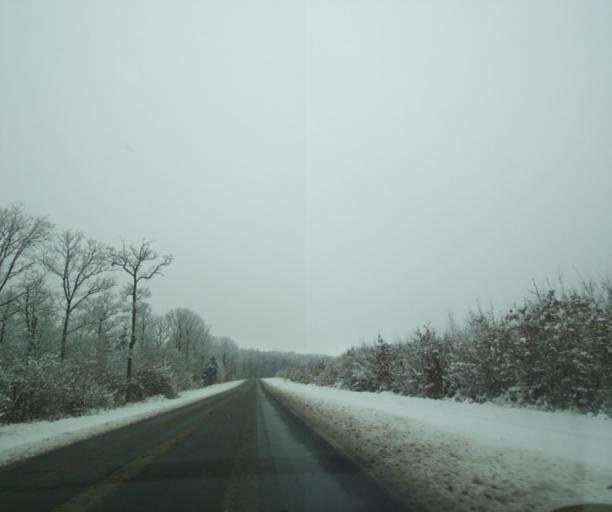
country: FR
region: Champagne-Ardenne
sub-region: Departement de la Haute-Marne
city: Laneuville-a-Remy
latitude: 48.5457
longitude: 4.8321
